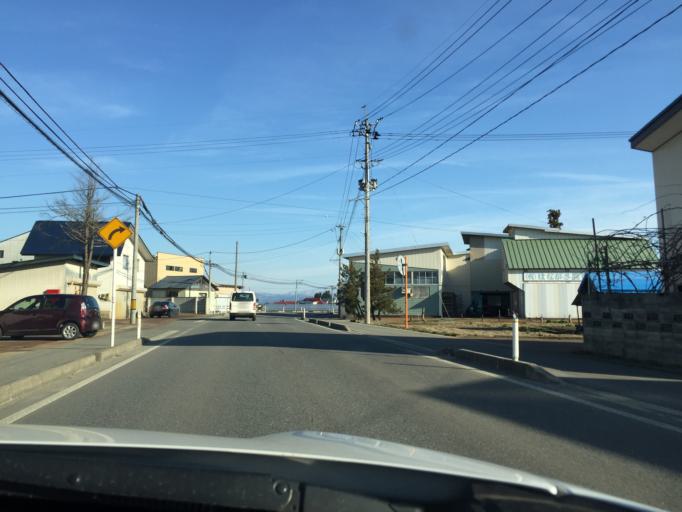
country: JP
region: Yamagata
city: Yonezawa
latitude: 37.9933
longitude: 140.0580
